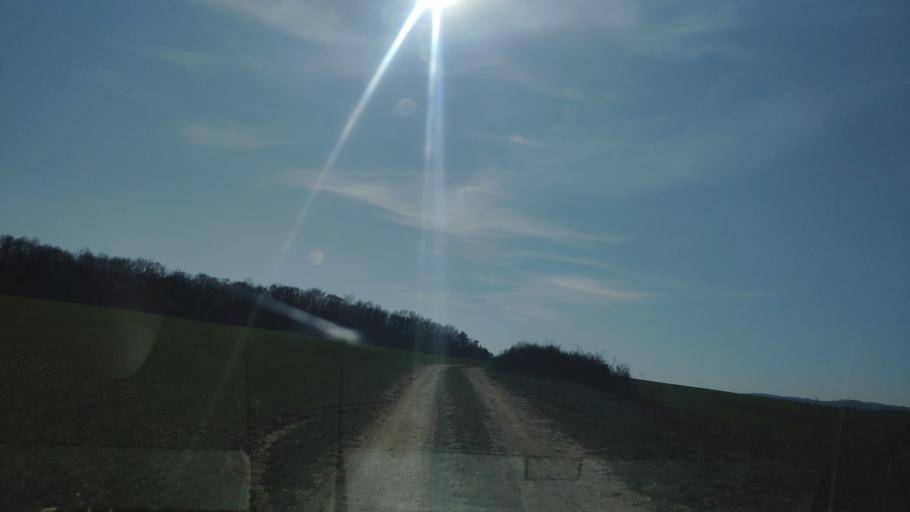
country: SK
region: Banskobystricky
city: Revuca
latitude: 48.5457
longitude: 20.2792
